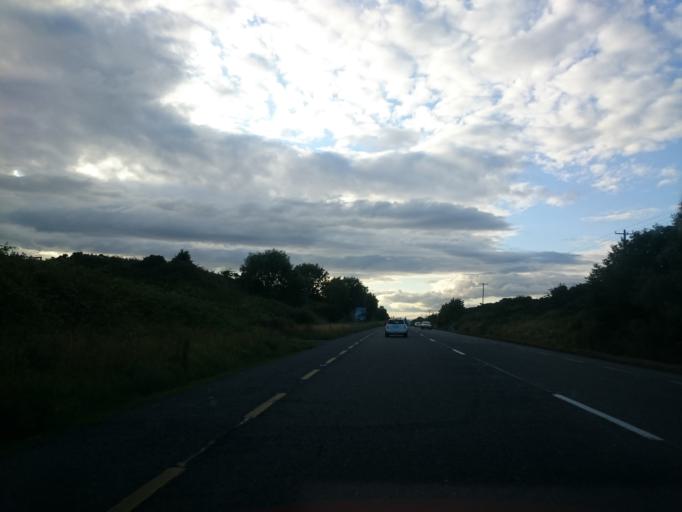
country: IE
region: Leinster
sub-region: Loch Garman
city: Loch Garman
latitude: 52.3171
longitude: -6.4949
